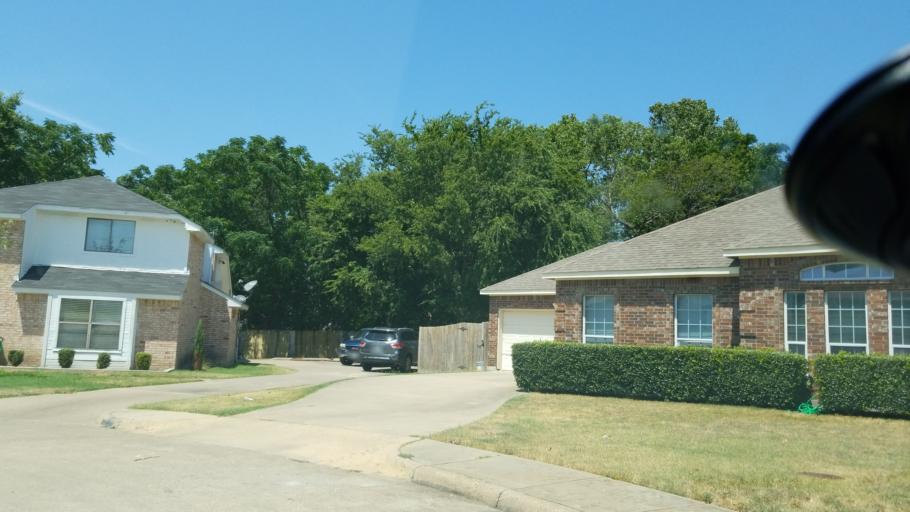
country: US
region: Texas
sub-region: Dallas County
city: Duncanville
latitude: 32.6381
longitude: -96.8886
